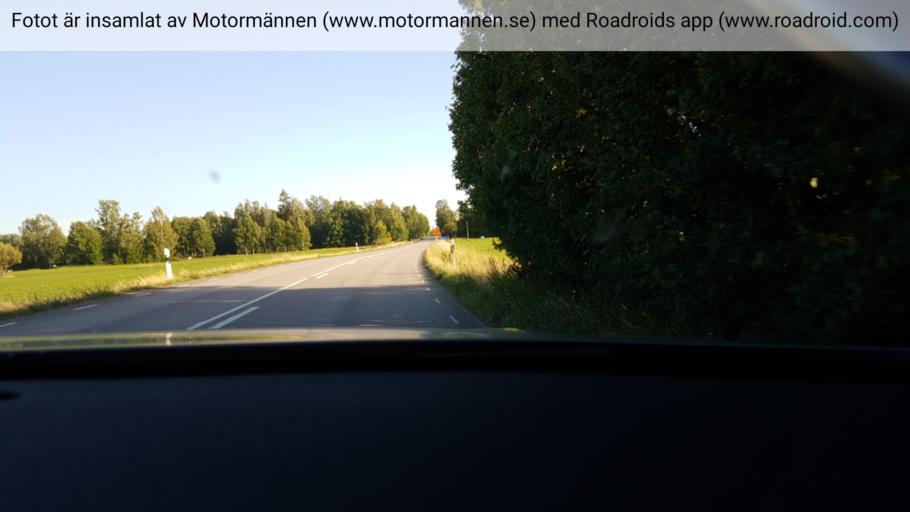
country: SE
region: Vaestra Goetaland
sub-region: Skovde Kommun
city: Stopen
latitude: 58.5071
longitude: 13.9711
